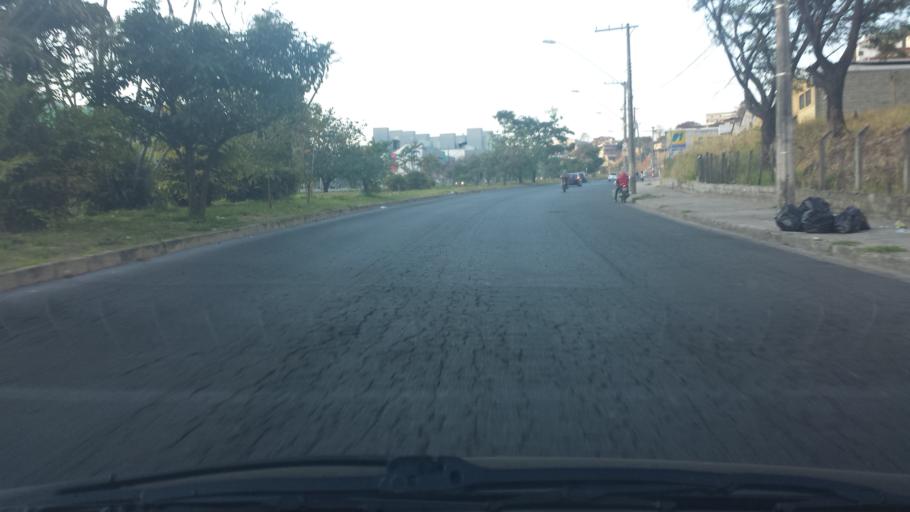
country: BR
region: Minas Gerais
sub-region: Belo Horizonte
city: Belo Horizonte
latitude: -19.8895
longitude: -43.9935
